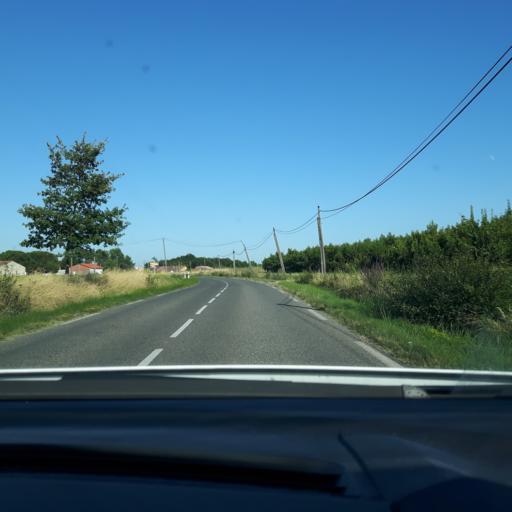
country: FR
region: Midi-Pyrenees
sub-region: Departement de la Haute-Garonne
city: Fronton
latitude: 43.8414
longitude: 1.3685
